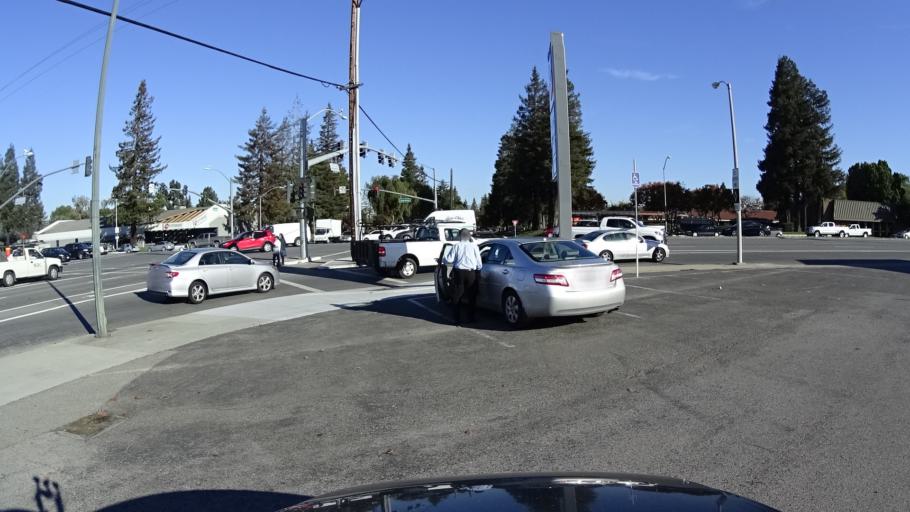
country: US
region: California
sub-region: Santa Clara County
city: Sunnyvale
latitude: 37.3803
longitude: -121.9964
